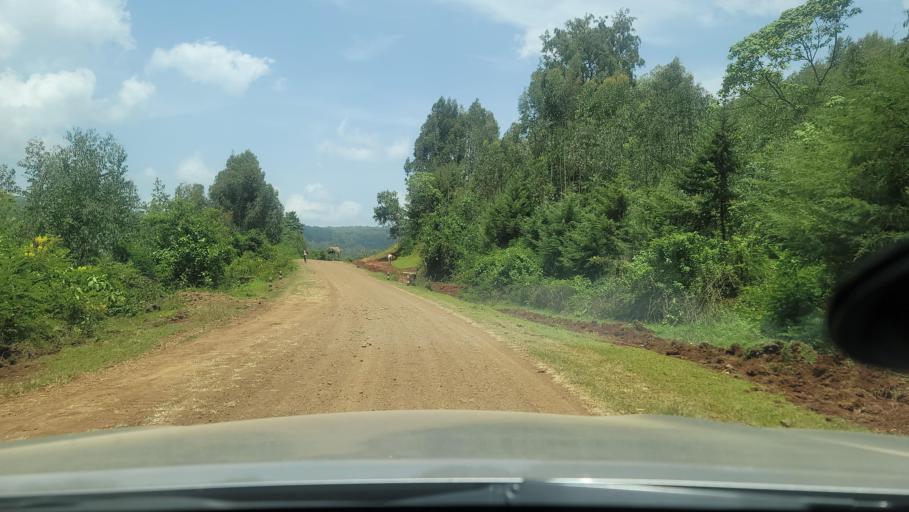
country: ET
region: Southern Nations, Nationalities, and People's Region
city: Bonga
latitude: 7.6987
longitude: 36.2476
